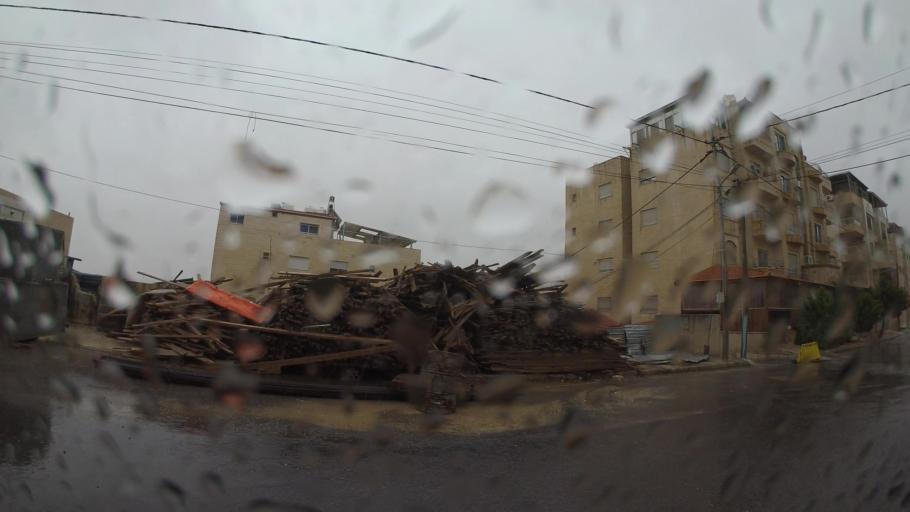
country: JO
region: Amman
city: Al Jubayhah
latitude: 32.0245
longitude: 35.8894
